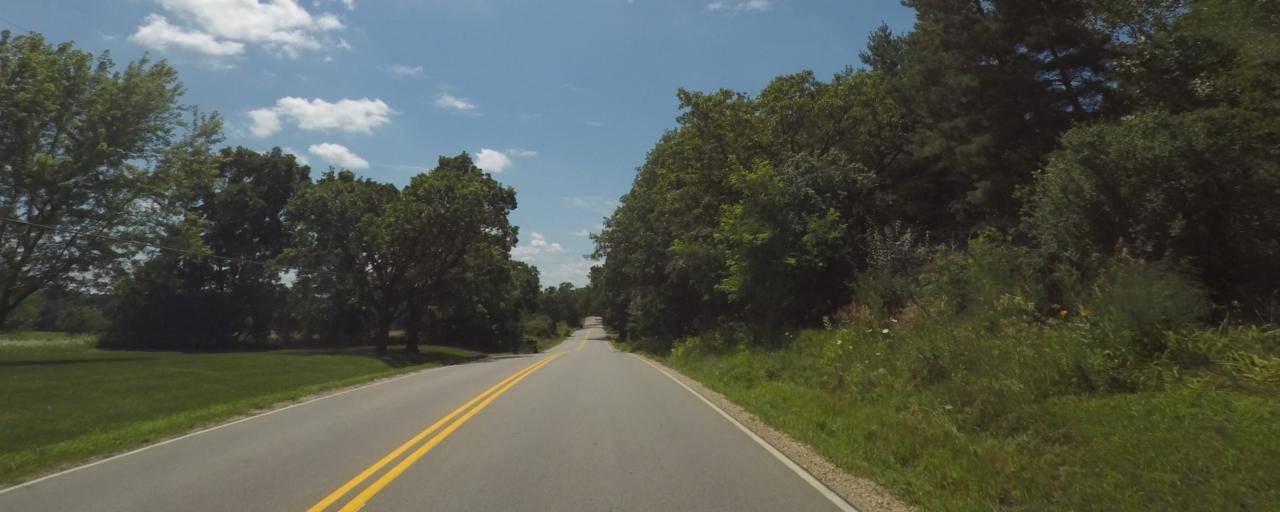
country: US
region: Wisconsin
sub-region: Waukesha County
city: Dousman
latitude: 42.9637
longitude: -88.4646
